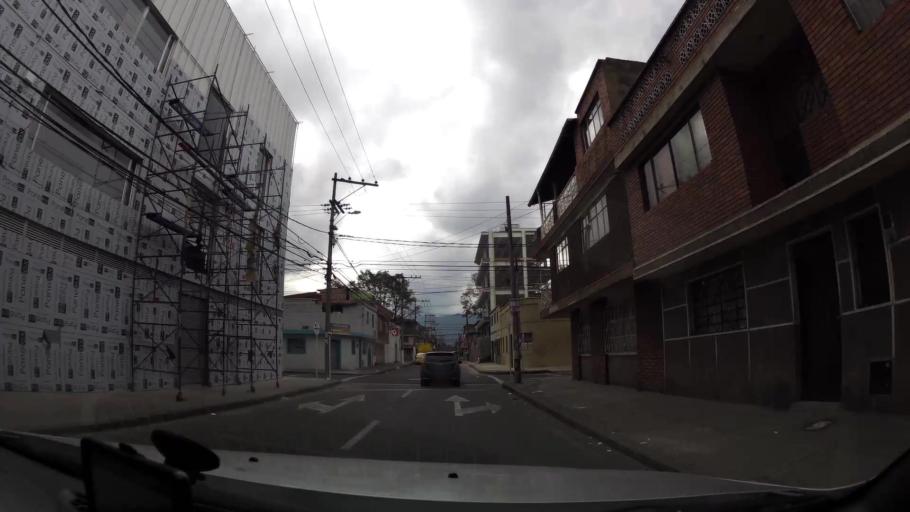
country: CO
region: Bogota D.C.
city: Bogota
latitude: 4.6270
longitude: -74.1217
